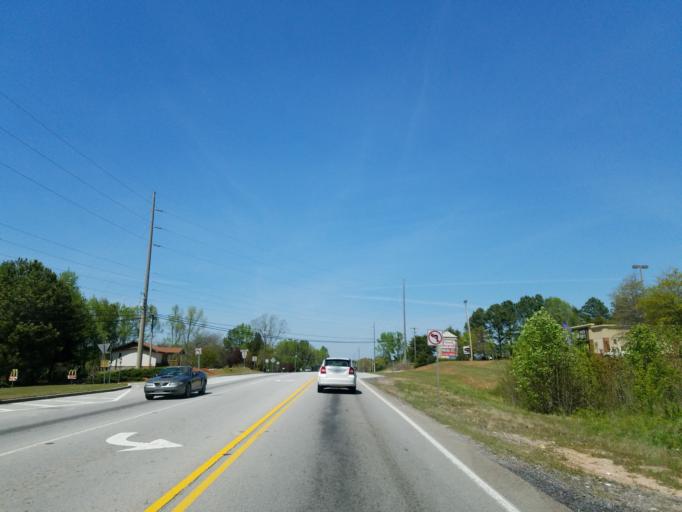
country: US
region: Georgia
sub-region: Paulding County
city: Dallas
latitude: 33.8677
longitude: -84.8416
